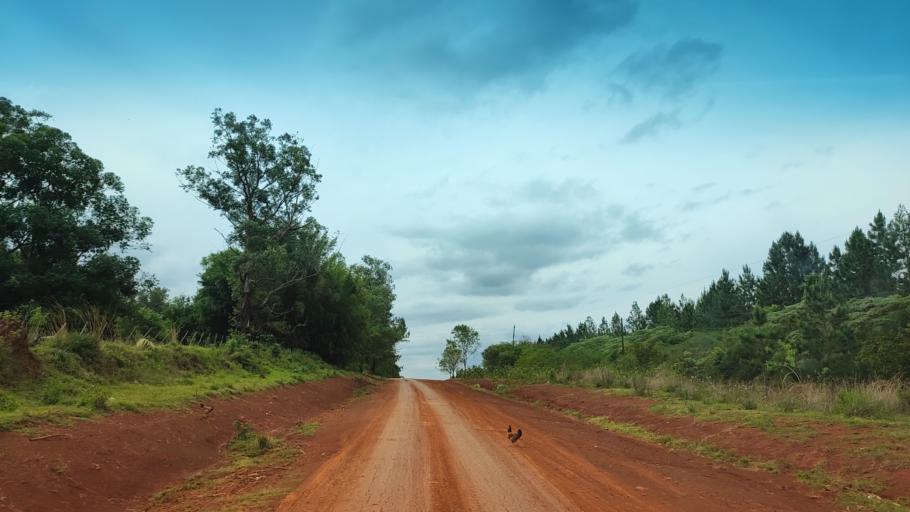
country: AR
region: Misiones
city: Garupa
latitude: -27.4956
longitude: -55.9708
